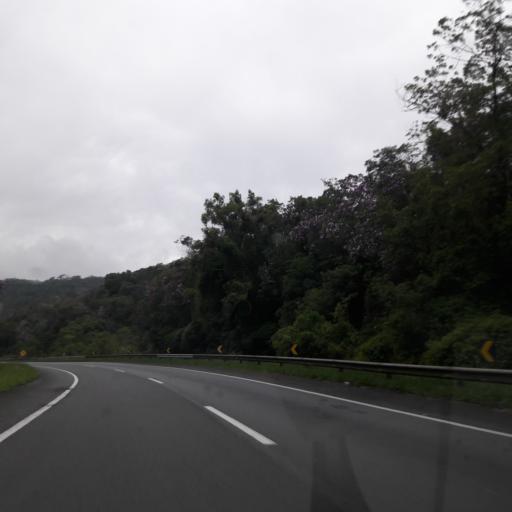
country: BR
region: Sao Paulo
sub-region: Cajati
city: Cajati
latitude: -24.9675
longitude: -48.4479
